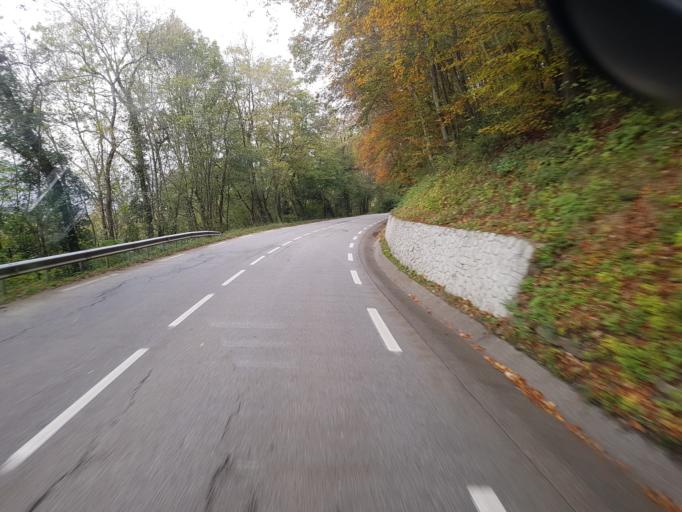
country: FR
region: Rhone-Alpes
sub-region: Departement de l'Isere
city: Le Gua
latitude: 44.9690
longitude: 5.6385
